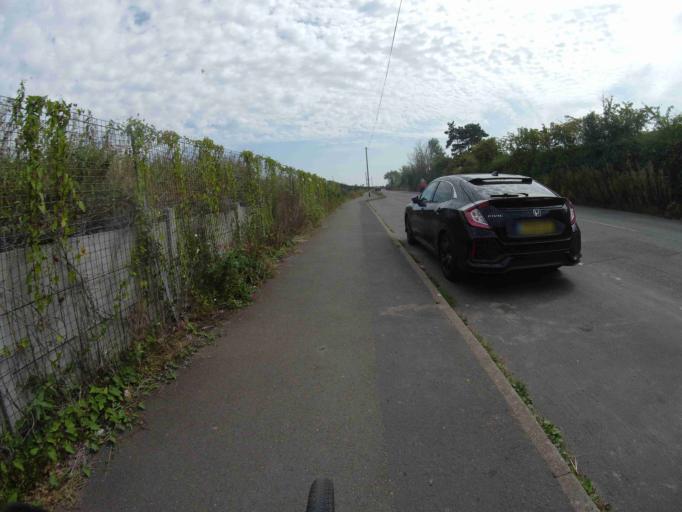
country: GB
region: England
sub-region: Devon
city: Starcross
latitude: 50.6143
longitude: -3.4460
